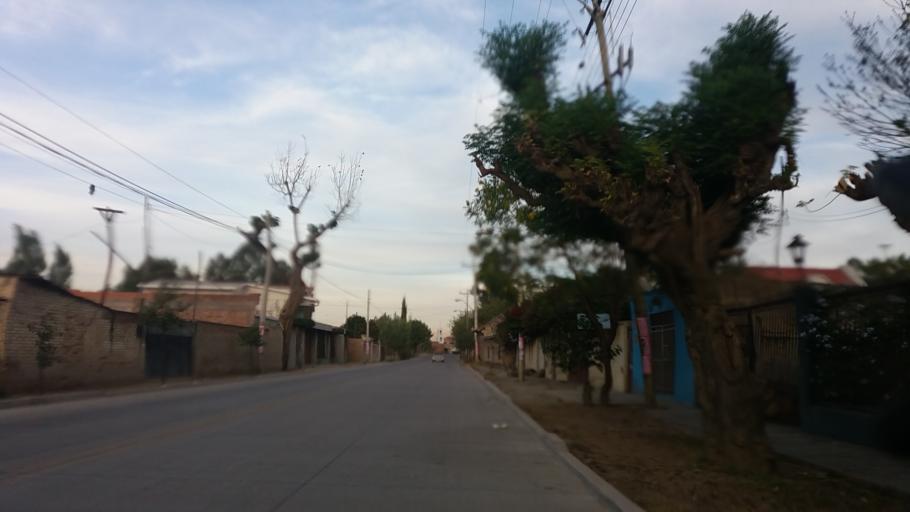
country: BO
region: Cochabamba
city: Cochabamba
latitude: -17.3693
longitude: -66.2089
